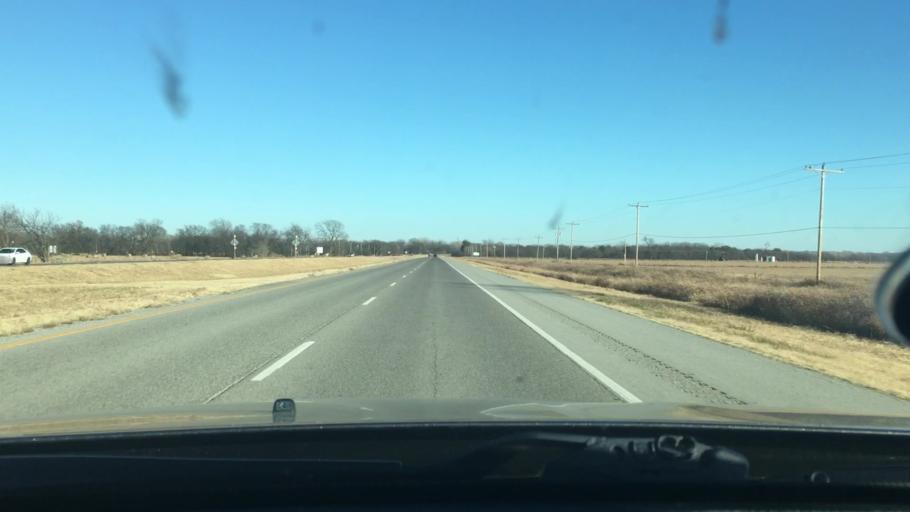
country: US
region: Oklahoma
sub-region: Murray County
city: Davis
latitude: 34.5064
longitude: -97.1646
